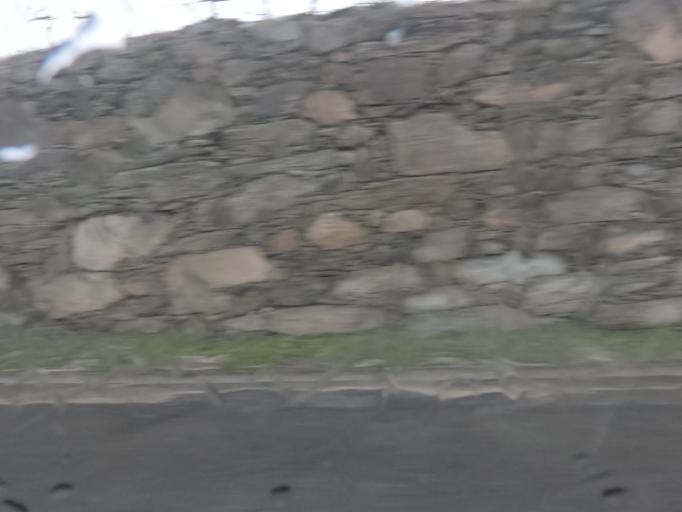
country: PT
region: Vila Real
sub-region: Peso da Regua
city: Peso da Regua
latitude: 41.1677
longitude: -7.7371
